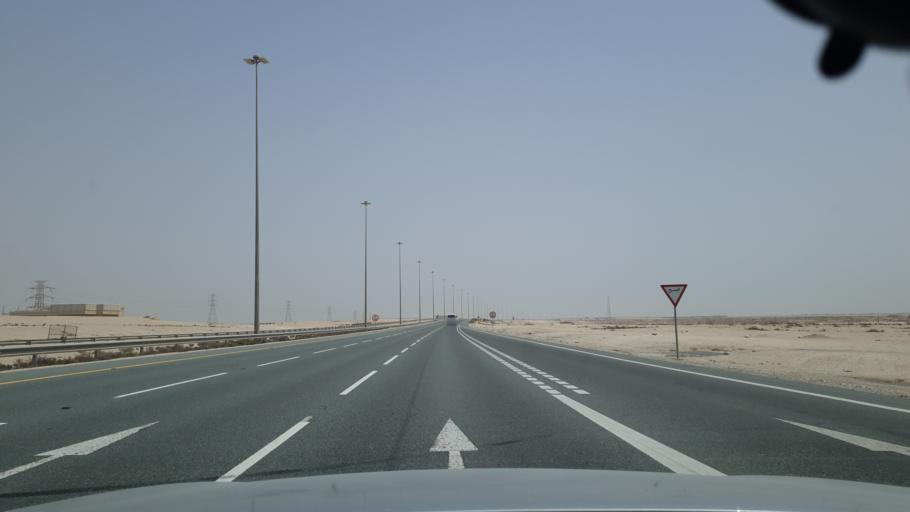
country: QA
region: Baladiyat ar Rayyan
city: Dukhan
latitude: 25.4606
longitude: 50.9005
